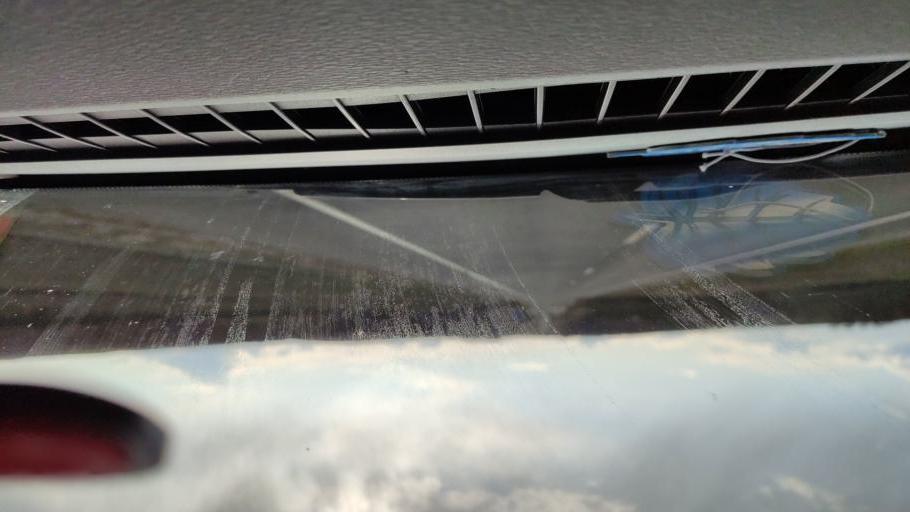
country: RU
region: Saratov
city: Yelshanka
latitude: 51.8256
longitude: 46.3892
